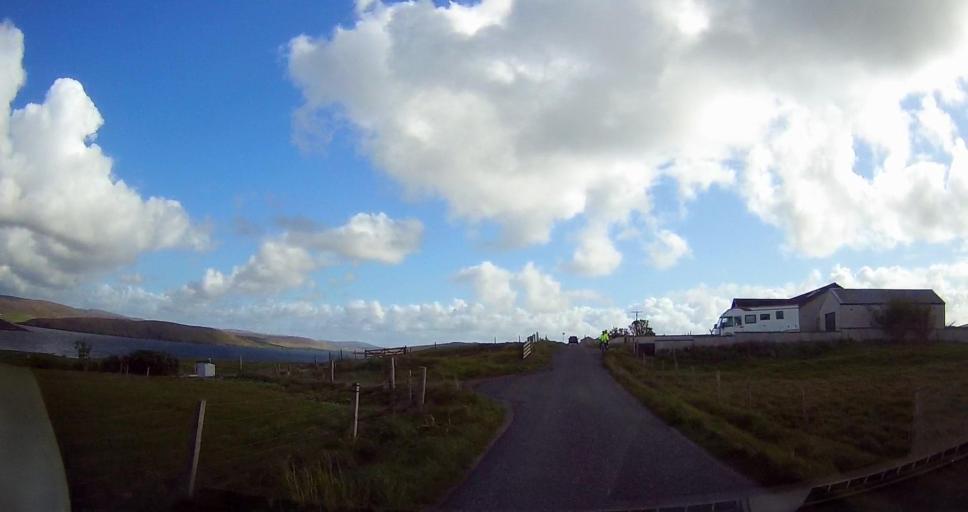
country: GB
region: Scotland
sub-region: Shetland Islands
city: Lerwick
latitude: 60.3631
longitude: -1.3823
